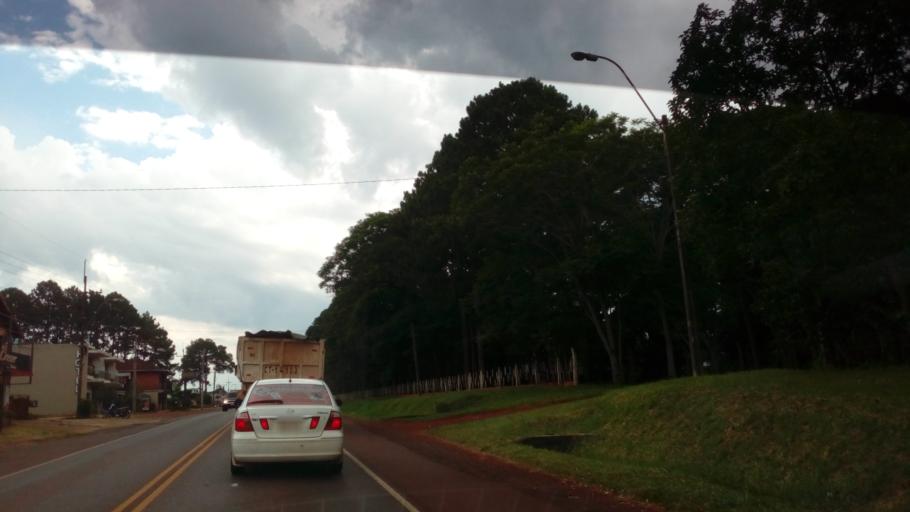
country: PY
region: Itapua
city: Obligado
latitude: -27.0759
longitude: -55.6423
